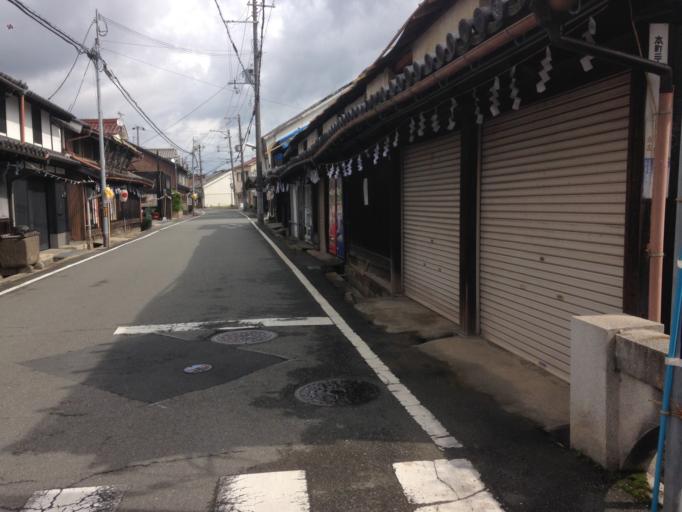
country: JP
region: Hyogo
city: Tatsunocho-tominaga
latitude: 34.8641
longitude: 134.5438
